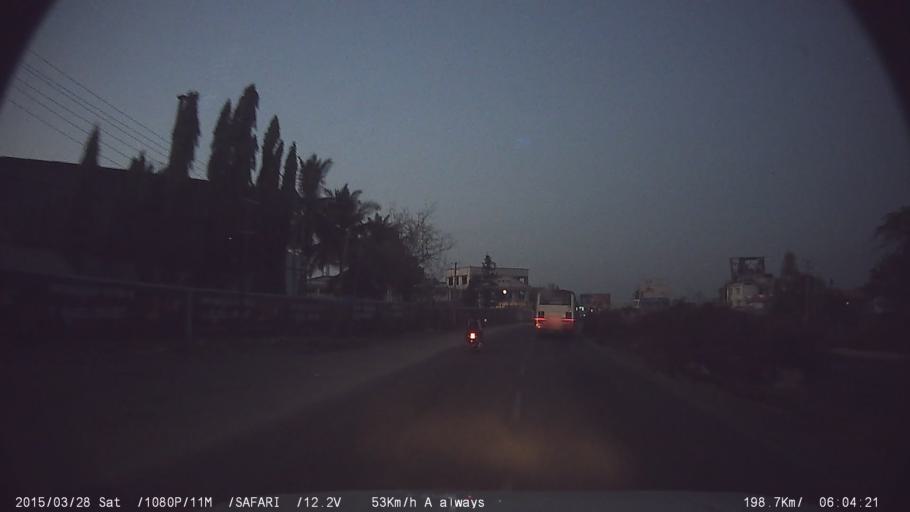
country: IN
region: Karnataka
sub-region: Ramanagara
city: Ramanagaram
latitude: 12.8334
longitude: 77.4141
